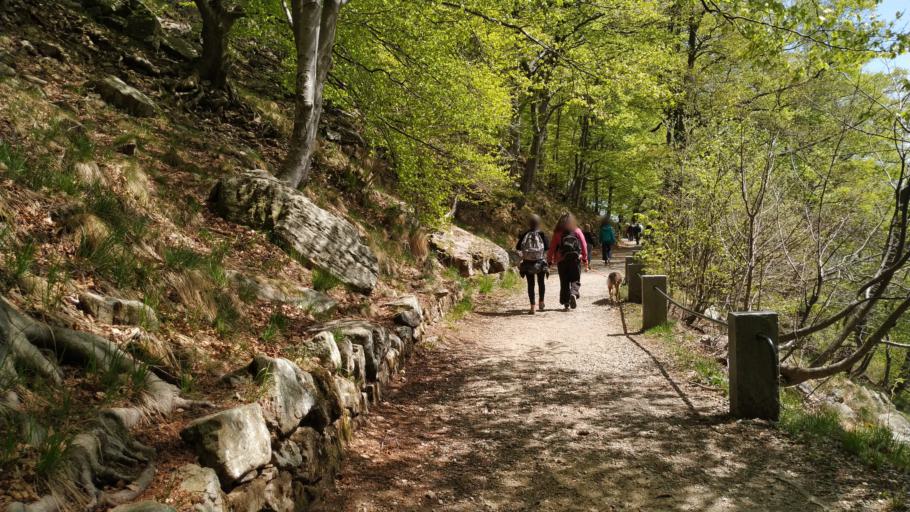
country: IT
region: Piedmont
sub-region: Provincia di Biella
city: San Paolo Cervo
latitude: 45.6287
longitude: 7.9826
